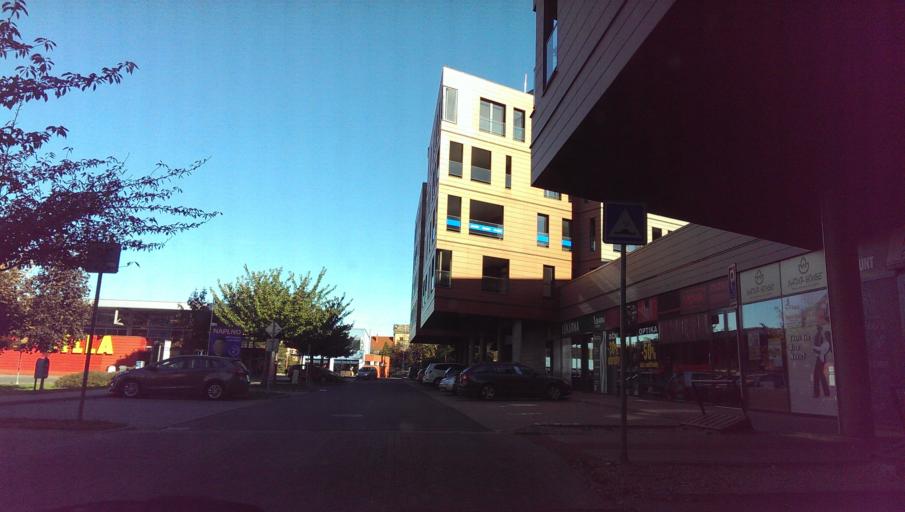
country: CZ
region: Zlin
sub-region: Okres Uherske Hradiste
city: Uherske Hradiste
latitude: 49.0697
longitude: 17.4629
